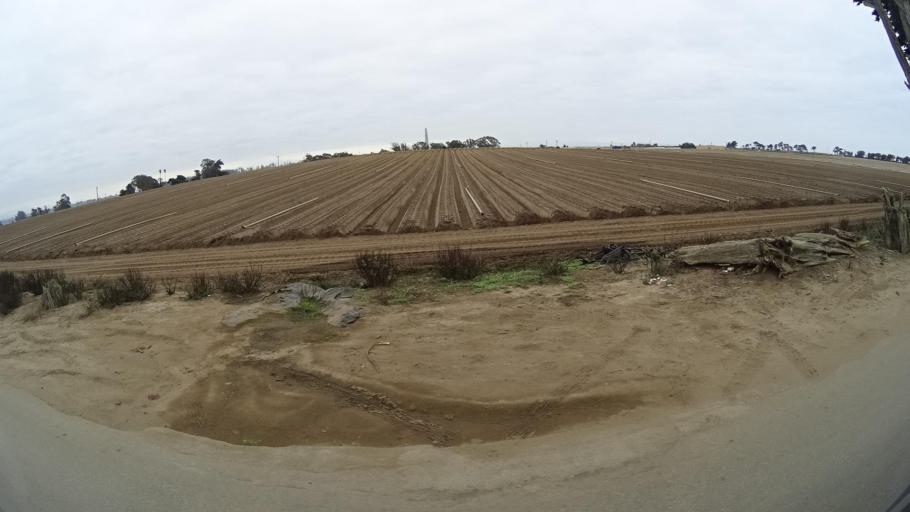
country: US
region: California
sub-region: Monterey County
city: Elkhorn
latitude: 36.8275
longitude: -121.7837
